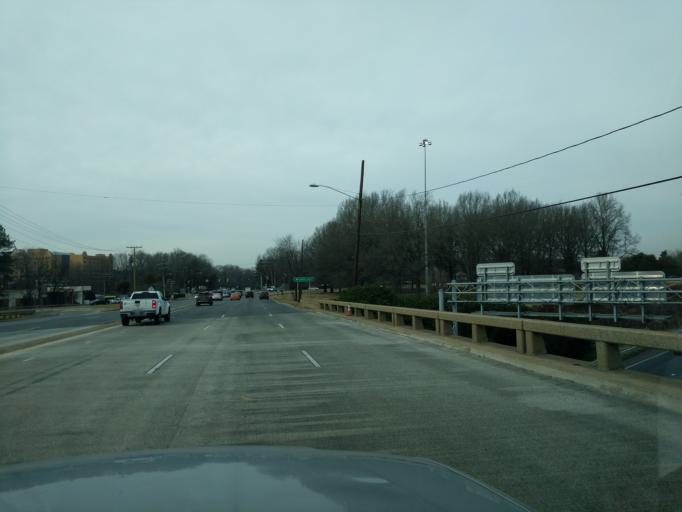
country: US
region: North Carolina
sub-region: Mecklenburg County
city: Charlotte
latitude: 35.1800
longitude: -80.8867
